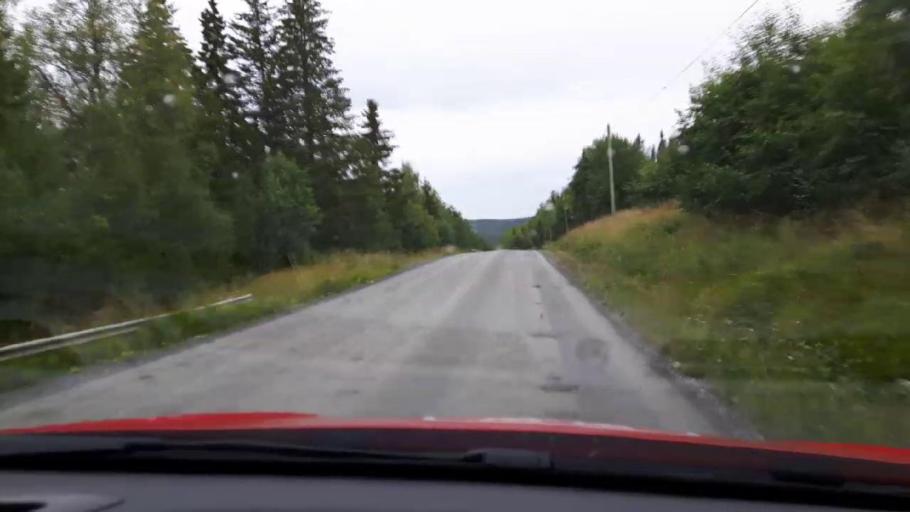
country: SE
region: Jaemtland
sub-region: Are Kommun
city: Jarpen
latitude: 63.4138
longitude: 13.3560
